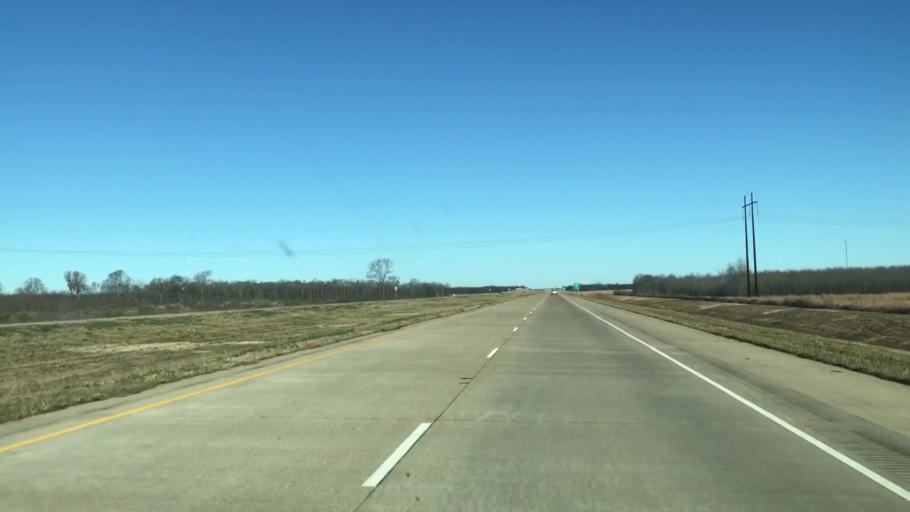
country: US
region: Louisiana
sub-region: Caddo Parish
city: Blanchard
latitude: 32.6649
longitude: -93.8459
